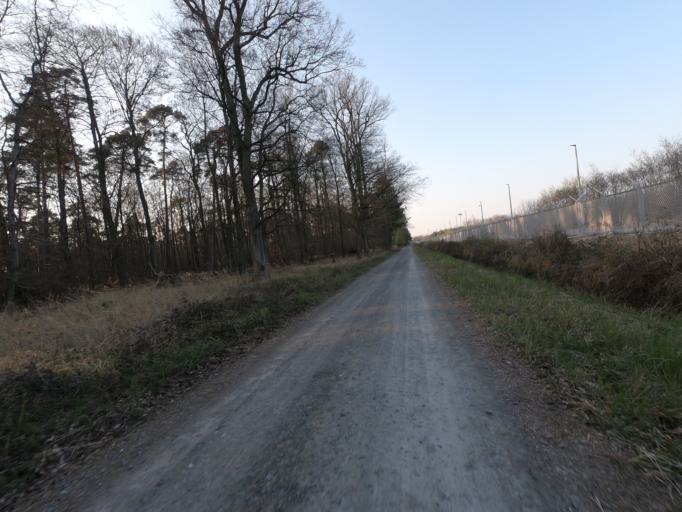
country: DE
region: Hesse
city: Kelsterbach
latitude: 50.0142
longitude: 8.5220
